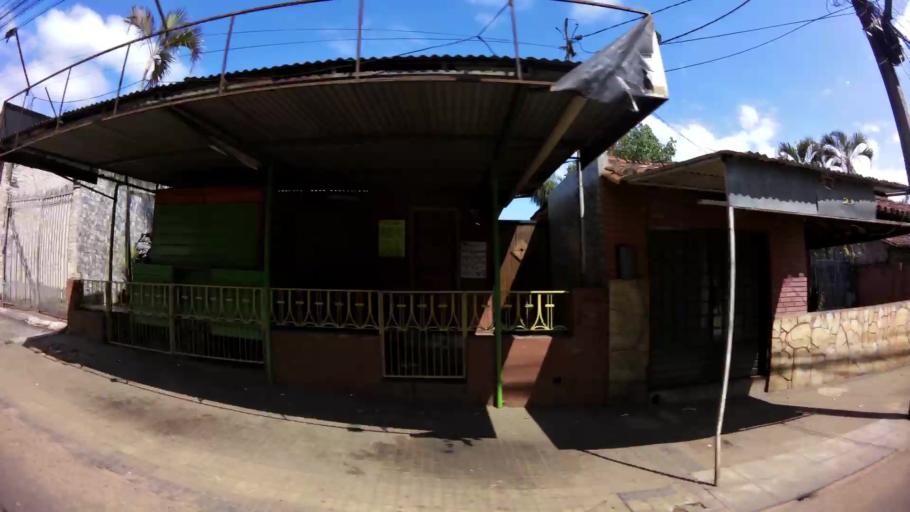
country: PY
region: Central
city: San Lorenzo
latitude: -25.2569
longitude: -57.4894
